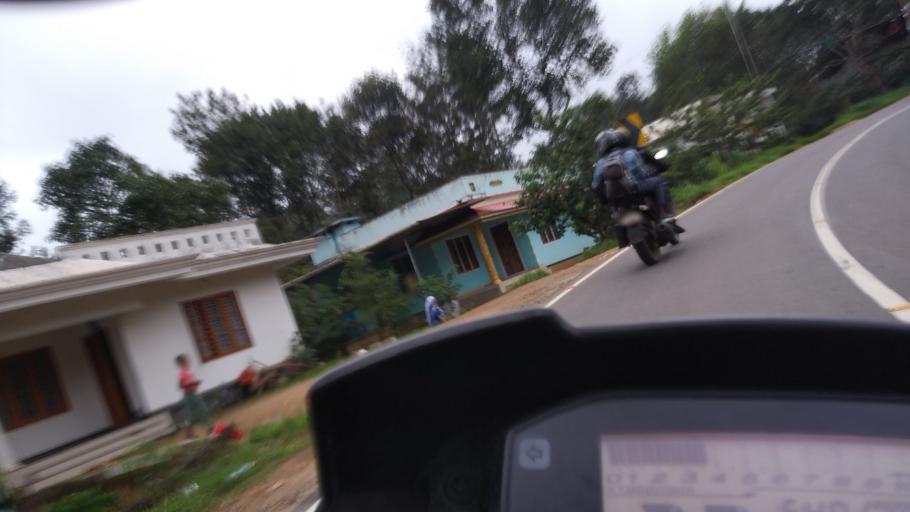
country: IN
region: Tamil Nadu
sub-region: Theni
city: Kombai
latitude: 9.9708
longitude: 77.1919
